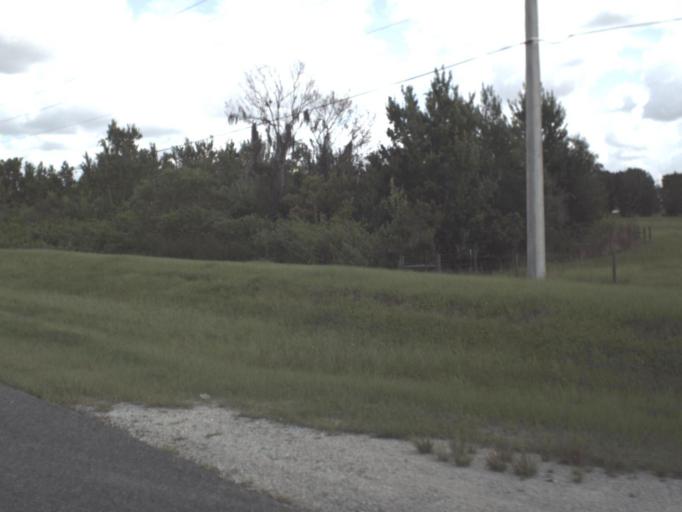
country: US
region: Florida
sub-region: Charlotte County
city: Harbour Heights
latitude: 27.0497
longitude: -81.9583
